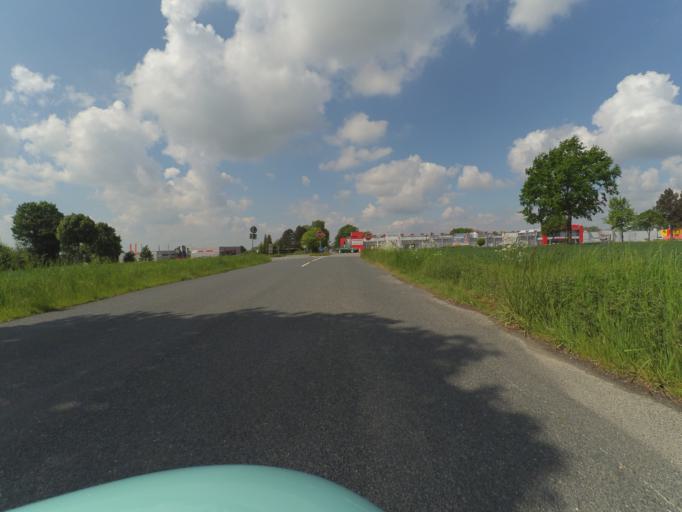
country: DE
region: Lower Saxony
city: Ilsede
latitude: 52.2453
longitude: 10.2297
